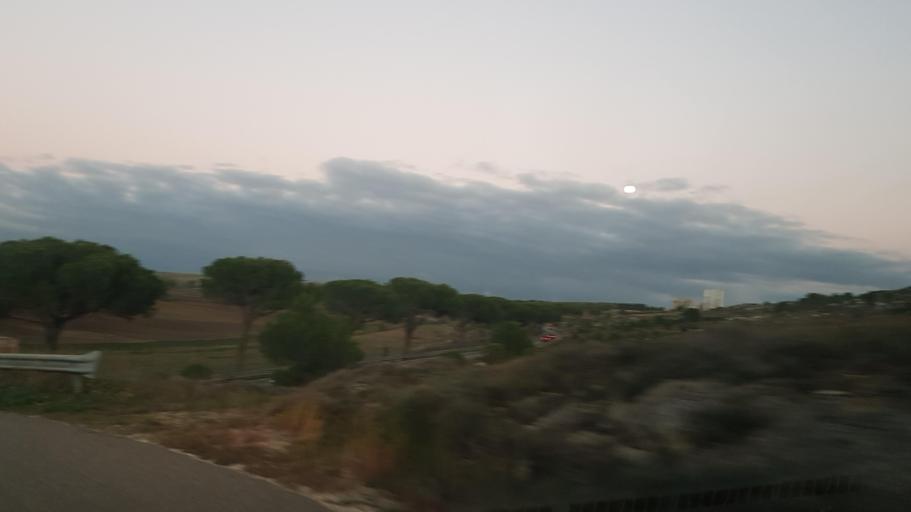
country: IT
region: Basilicate
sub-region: Provincia di Matera
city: Matera
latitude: 40.6769
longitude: 16.6313
